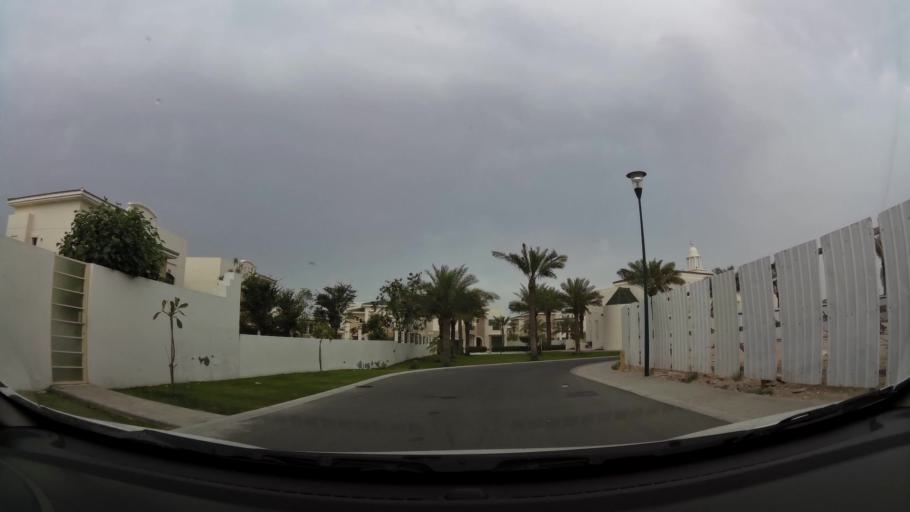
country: BH
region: Northern
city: Ar Rifa'
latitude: 26.0851
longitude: 50.5560
